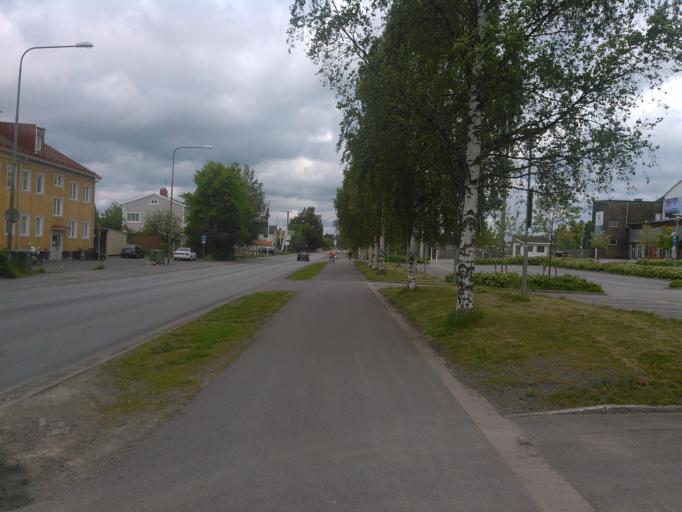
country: SE
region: Vaesterbotten
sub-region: Umea Kommun
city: Umea
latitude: 63.8283
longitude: 20.2848
